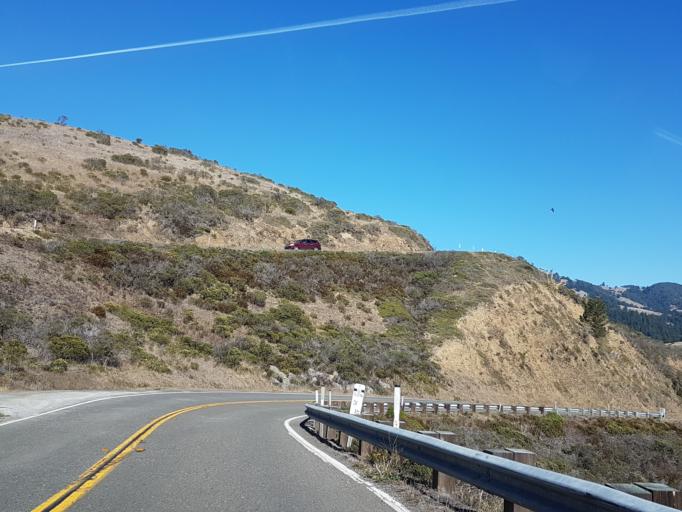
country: US
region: California
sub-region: Sonoma County
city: Monte Rio
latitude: 38.4713
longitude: -123.1588
